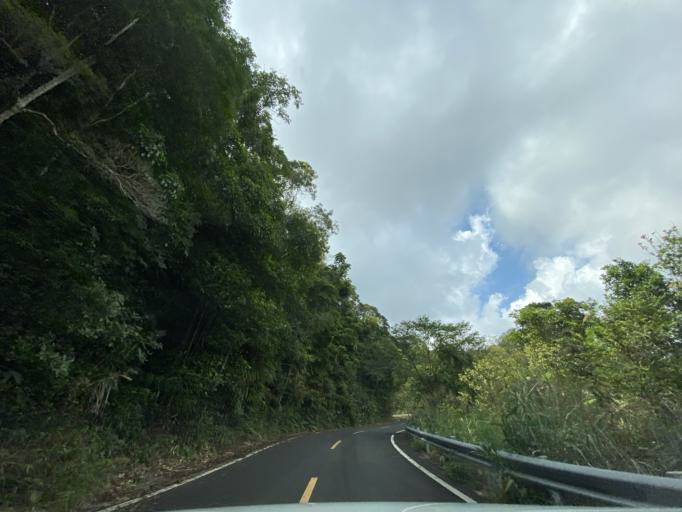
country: CN
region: Hainan
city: Diaoluoshan
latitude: 18.7130
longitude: 109.8808
